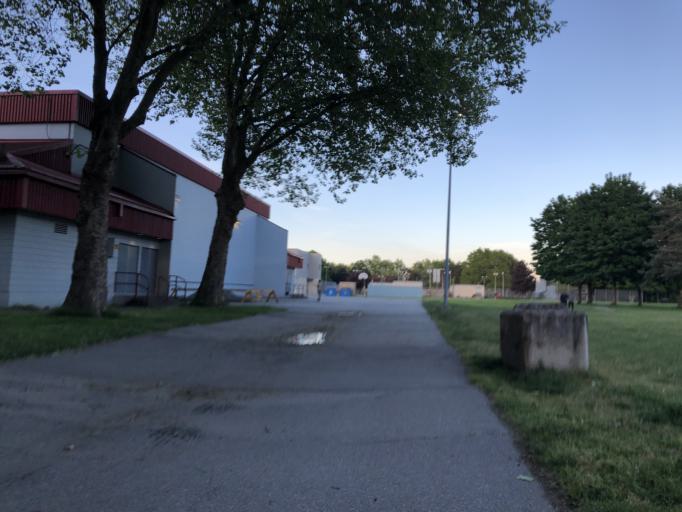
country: CA
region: British Columbia
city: Richmond
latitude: 49.1396
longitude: -123.1282
